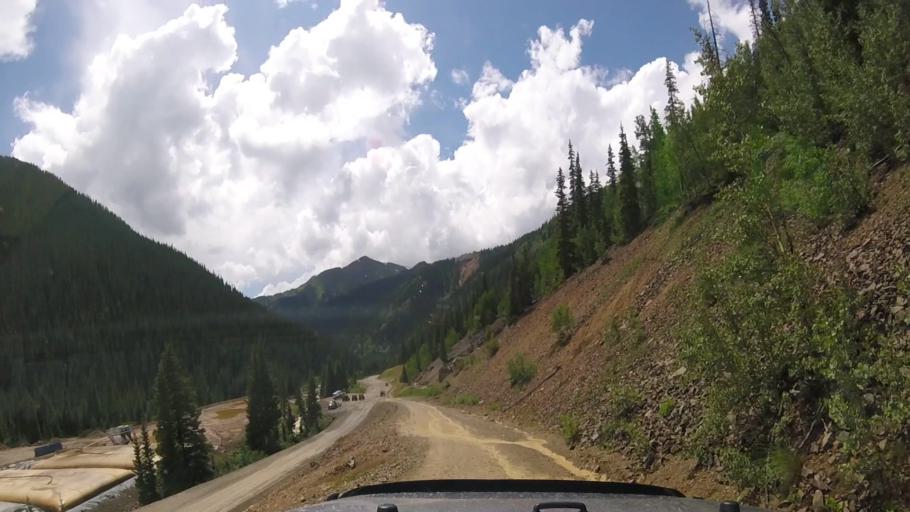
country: US
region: Colorado
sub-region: San Juan County
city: Silverton
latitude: 37.8909
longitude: -107.6504
